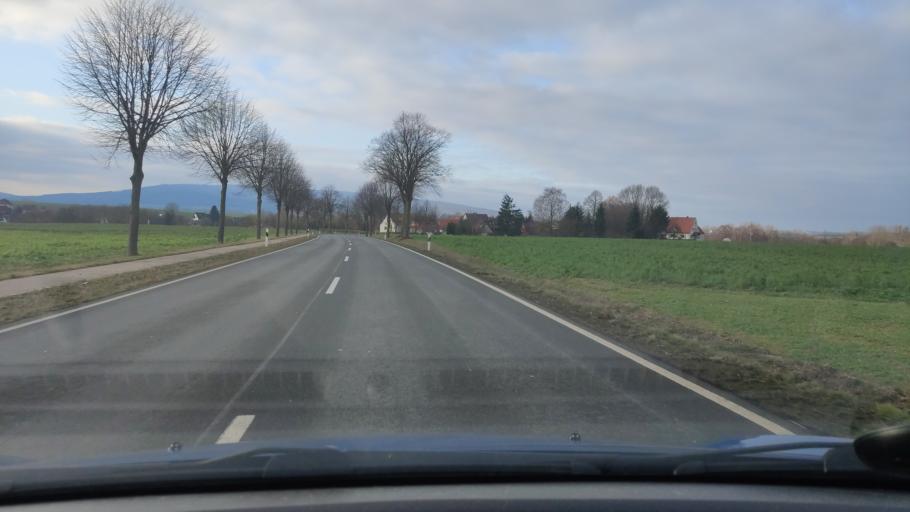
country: DE
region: Lower Saxony
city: Coppenbrugge
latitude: 52.1497
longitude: 9.5040
